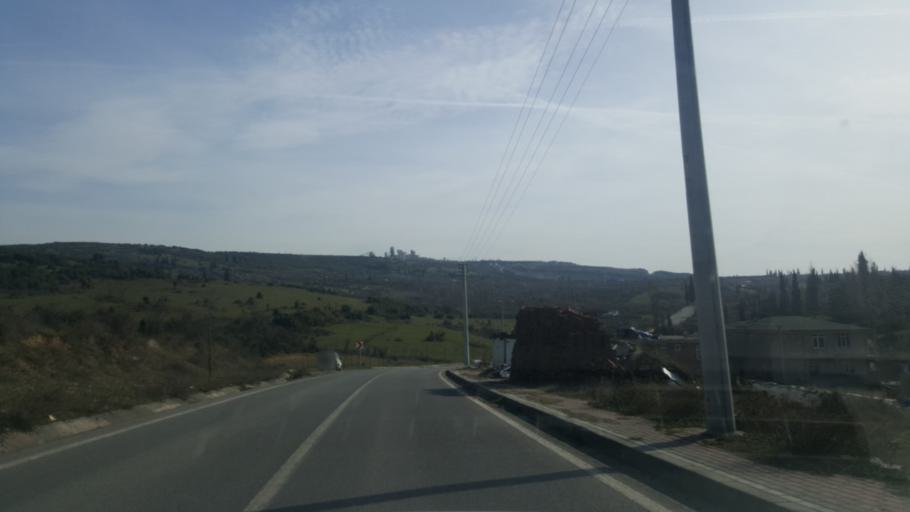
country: TR
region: Kocaeli
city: Tavsancil
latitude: 40.7890
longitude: 29.5651
